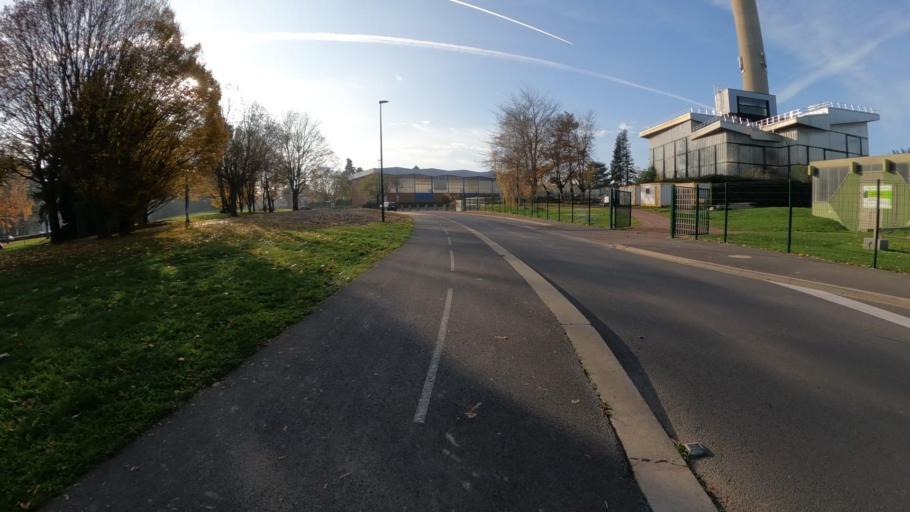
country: FR
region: Lower Normandy
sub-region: Departement du Calvados
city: Herouville-Saint-Clair
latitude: 49.2090
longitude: -0.3346
